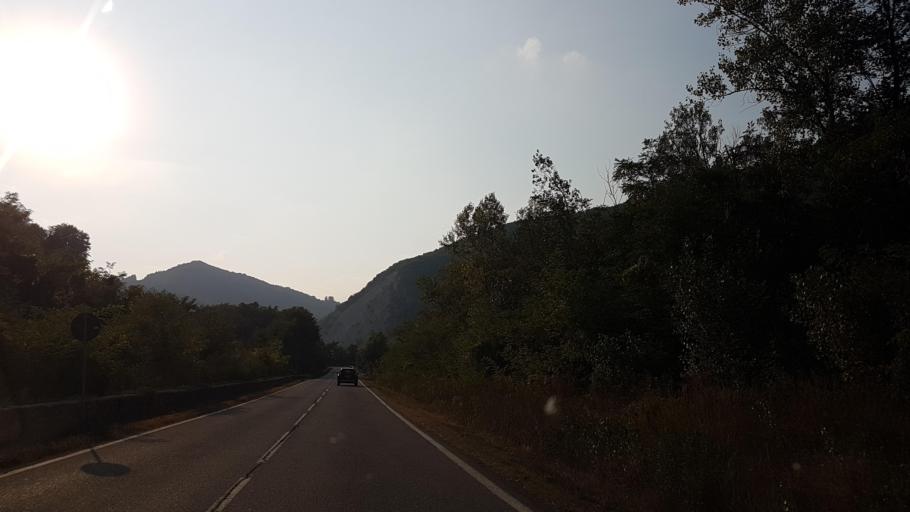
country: IT
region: Emilia-Romagna
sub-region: Provincia di Parma
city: Solignano
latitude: 44.6287
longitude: 10.0175
